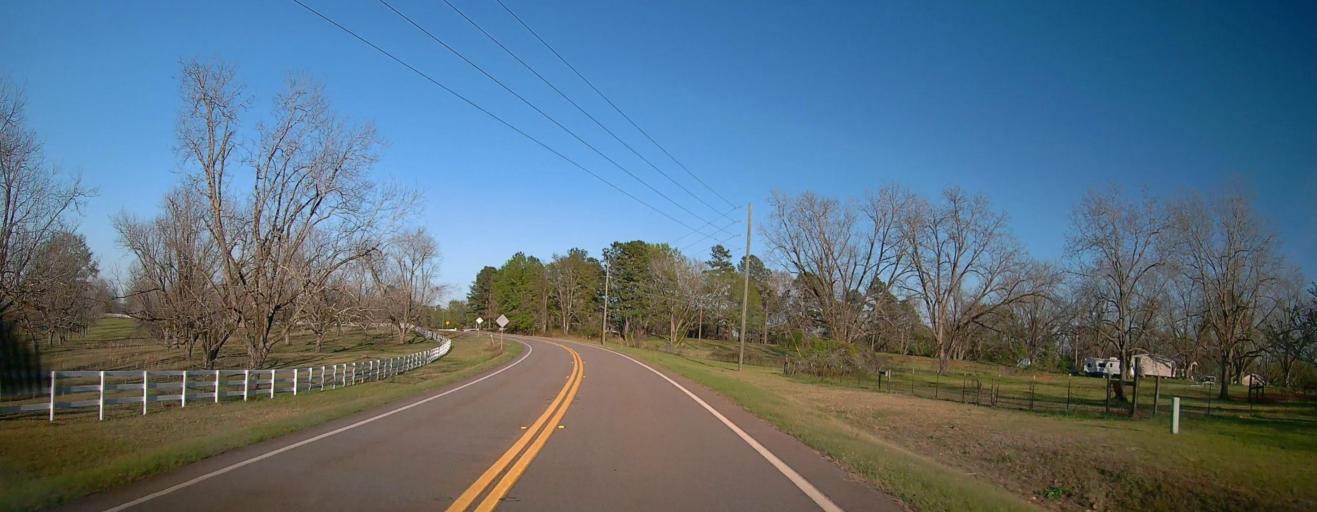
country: US
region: Georgia
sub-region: Wilkinson County
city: Irwinton
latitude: 32.8707
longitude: -83.1120
